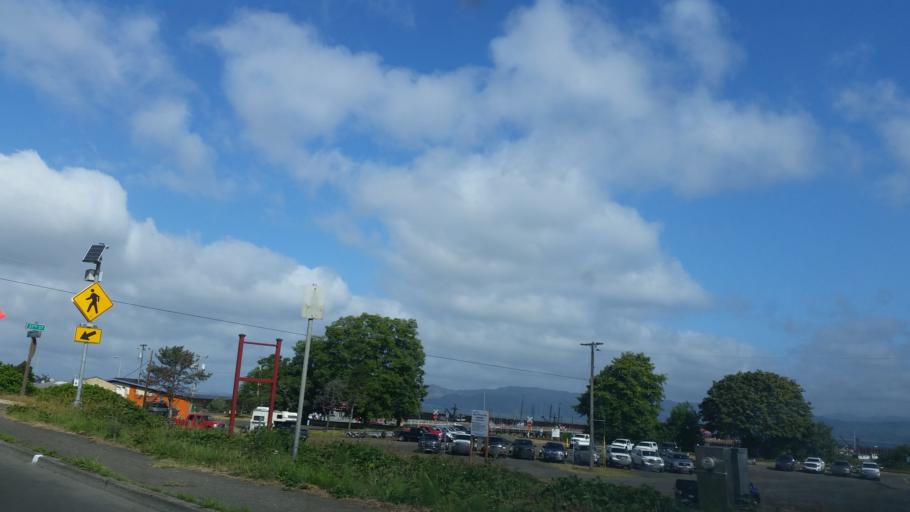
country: US
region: Oregon
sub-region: Clatsop County
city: Astoria
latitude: 46.1935
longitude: -123.8009
